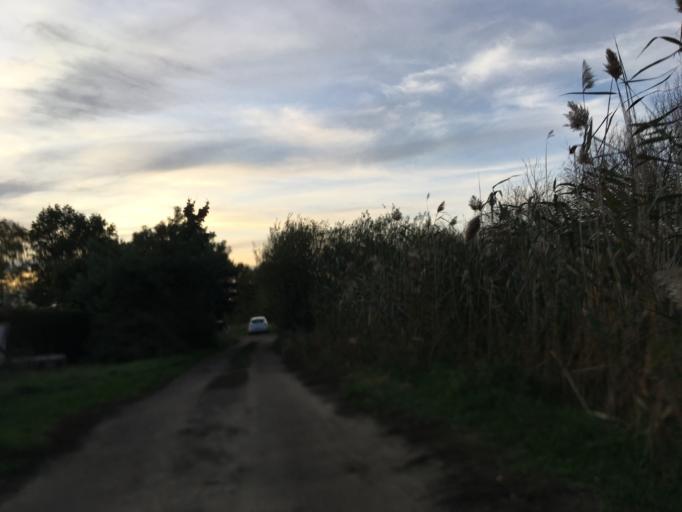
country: DE
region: Berlin
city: Buchholz
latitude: 52.6192
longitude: 13.4357
